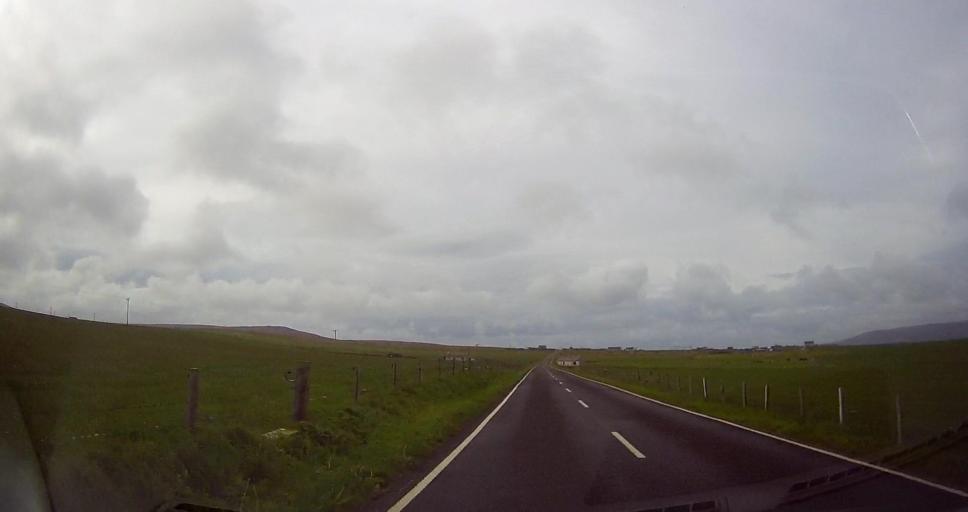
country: GB
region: Scotland
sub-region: Orkney Islands
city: Stromness
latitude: 58.9636
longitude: -3.2242
